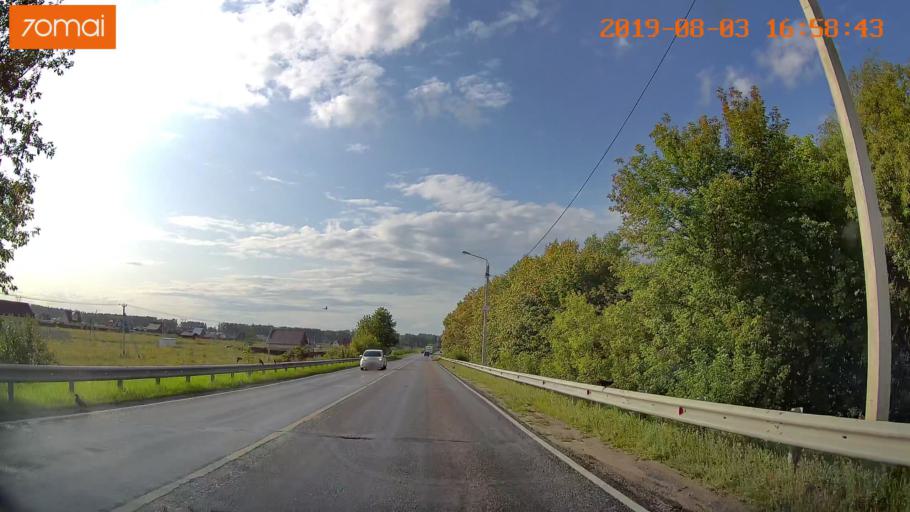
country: RU
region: Moskovskaya
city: Voskresensk
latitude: 55.3238
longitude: 38.6315
